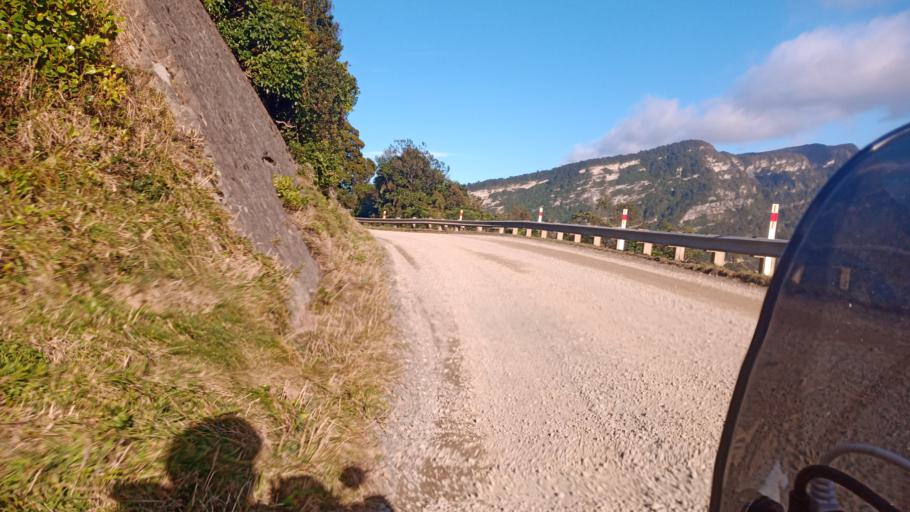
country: NZ
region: Hawke's Bay
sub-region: Wairoa District
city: Wairoa
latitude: -38.7881
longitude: 177.1294
